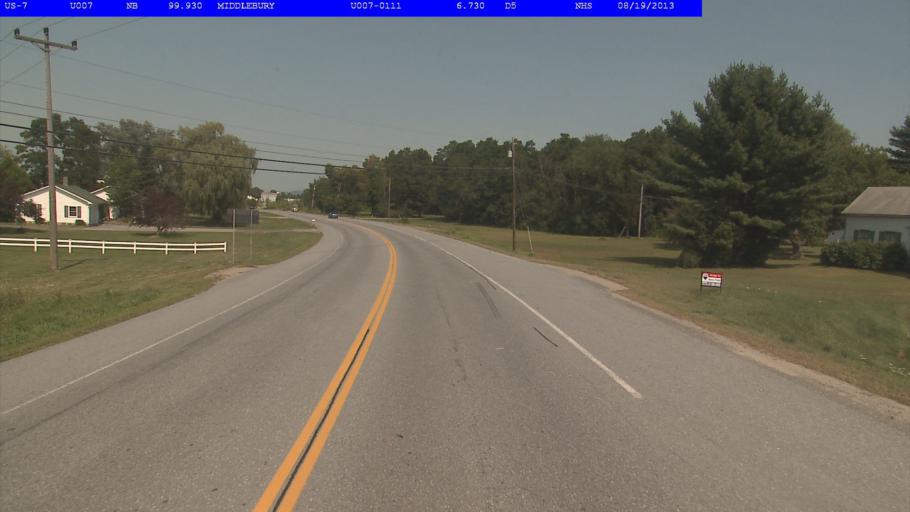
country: US
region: Vermont
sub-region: Addison County
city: Middlebury (village)
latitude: 44.0363
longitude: -73.1619
